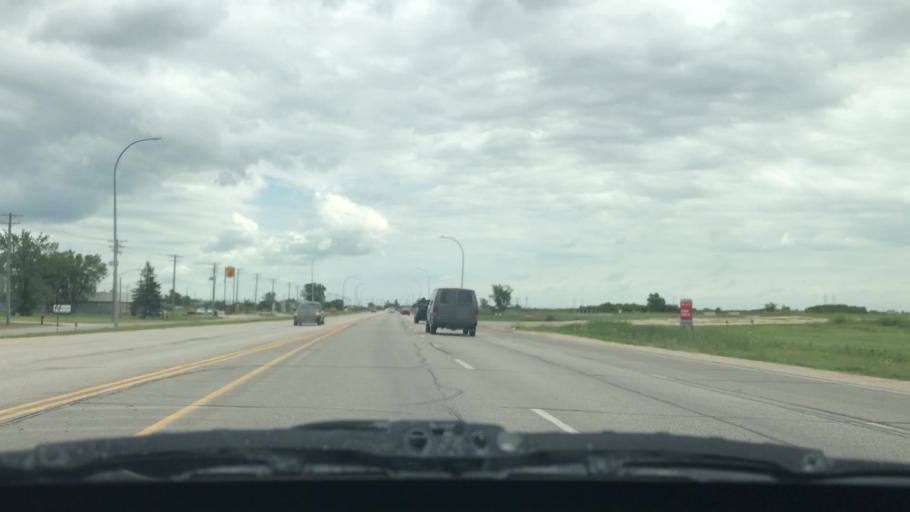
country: CA
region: Manitoba
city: Winnipeg
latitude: 49.8560
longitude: -97.0446
